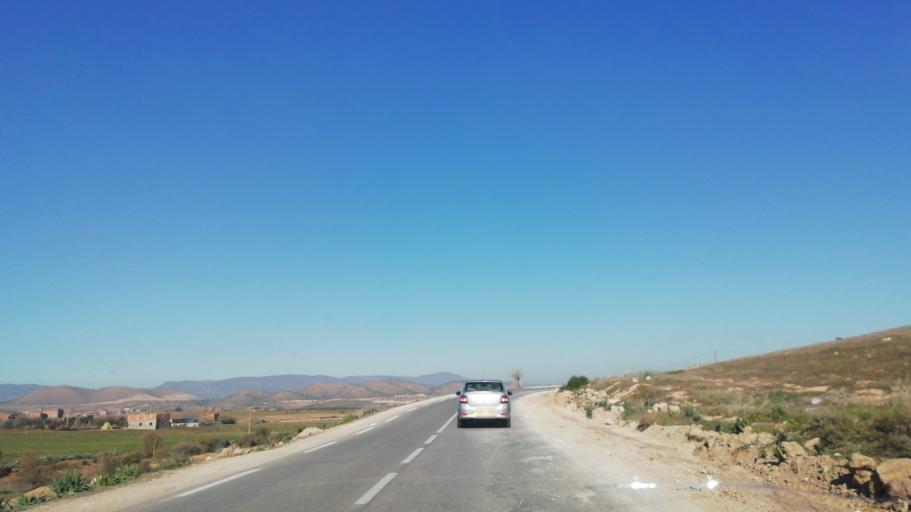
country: DZ
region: Tlemcen
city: Nedroma
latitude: 34.8335
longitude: -1.6863
